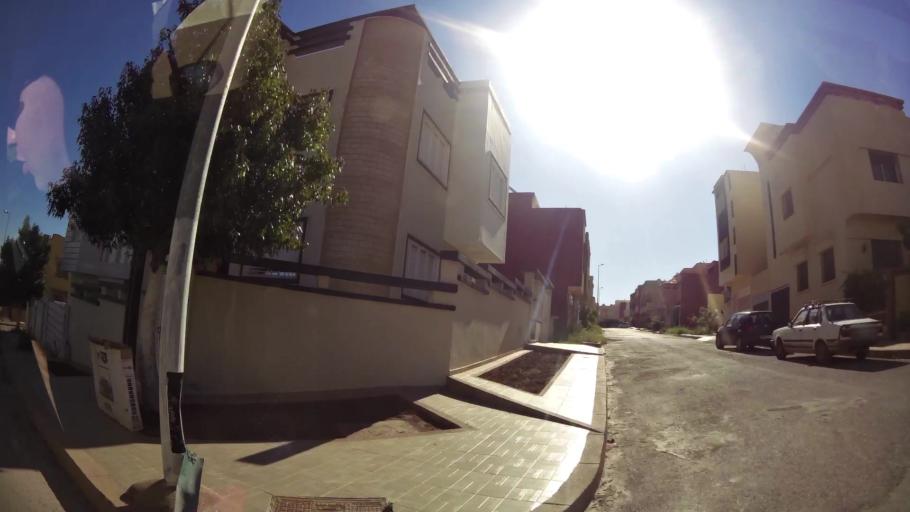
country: MA
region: Oriental
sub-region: Oujda-Angad
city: Oujda
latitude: 34.6464
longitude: -1.8909
